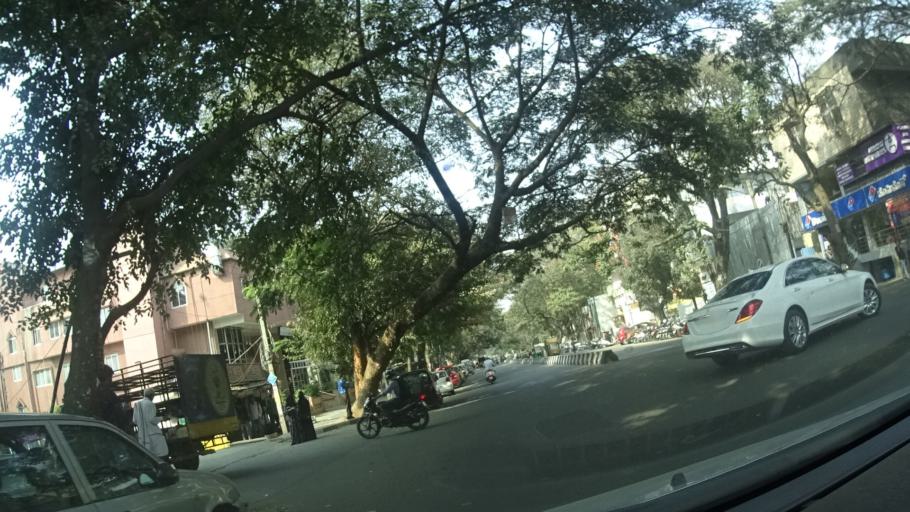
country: IN
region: Karnataka
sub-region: Bangalore Urban
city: Bangalore
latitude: 12.9447
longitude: 77.5678
